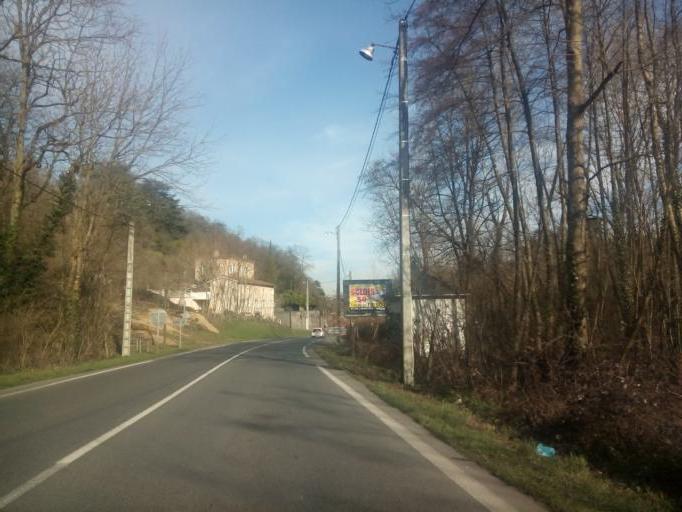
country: FR
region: Rhone-Alpes
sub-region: Departement du Rhone
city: Francheville
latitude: 45.7155
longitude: 4.7760
